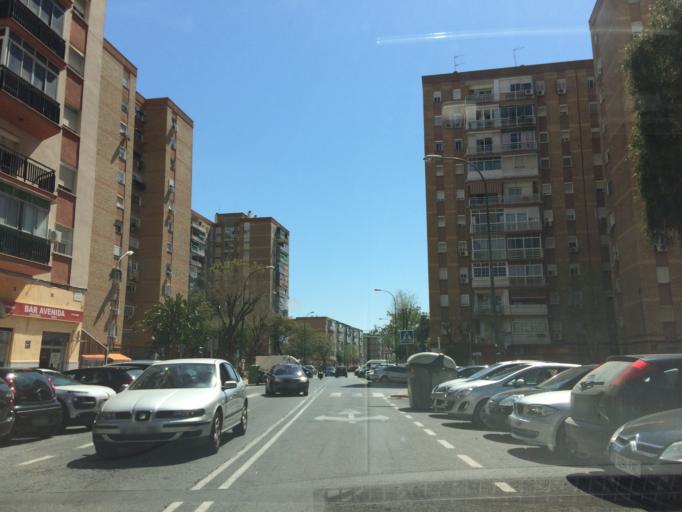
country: ES
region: Andalusia
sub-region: Provincia de Malaga
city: Malaga
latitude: 36.6916
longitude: -4.4545
